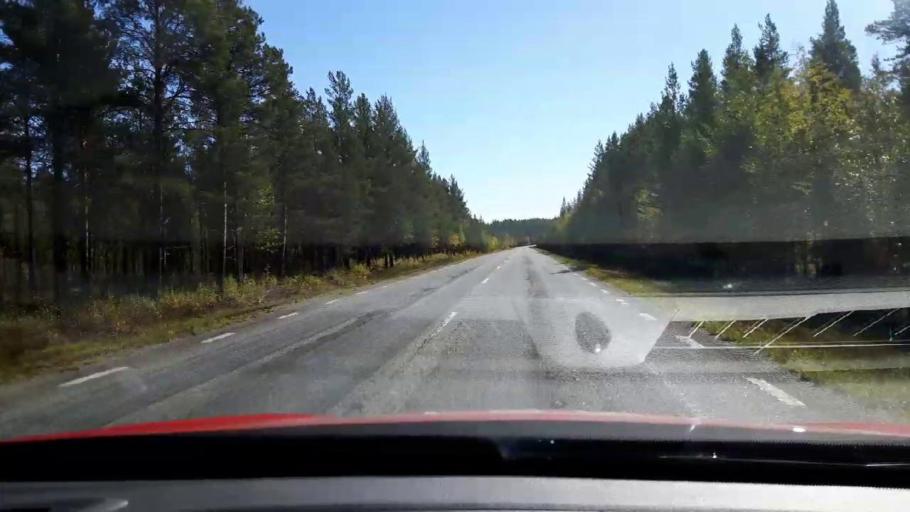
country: SE
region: Jaemtland
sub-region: Harjedalens Kommun
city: Sveg
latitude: 62.3376
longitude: 14.0452
